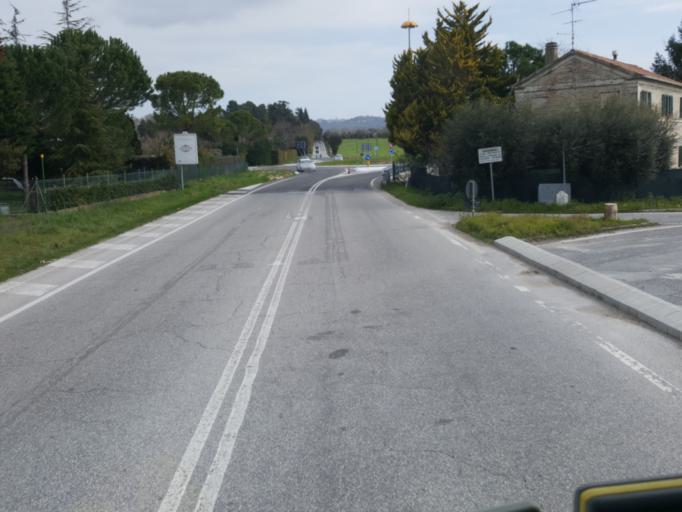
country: IT
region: The Marches
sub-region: Provincia di Macerata
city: Recanati
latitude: 43.3653
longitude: 13.5122
